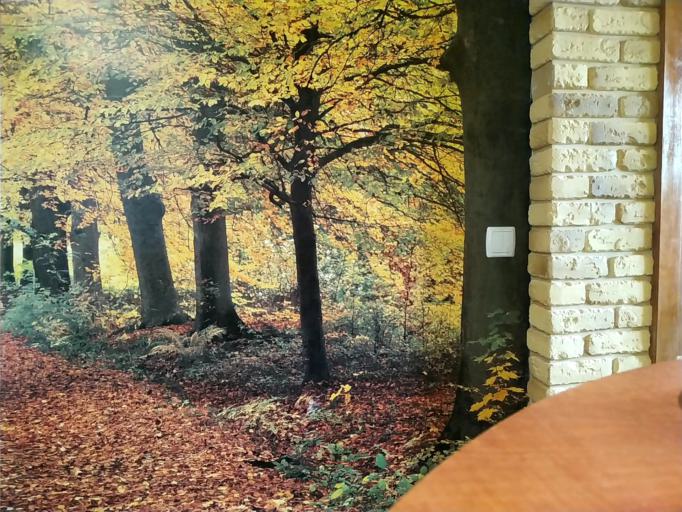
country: RU
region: Novgorod
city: Opechenskiy Posad
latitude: 58.2694
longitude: 34.0148
